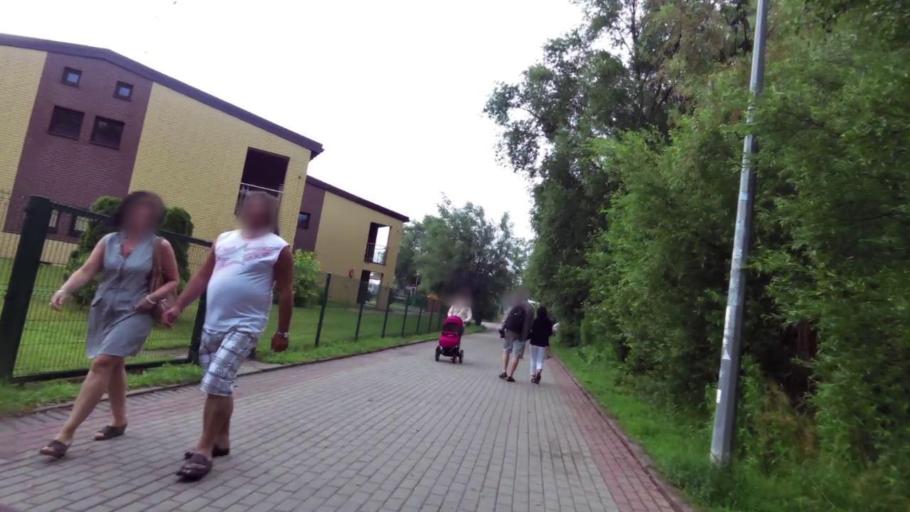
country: PL
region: West Pomeranian Voivodeship
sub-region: Powiat kolobrzeski
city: Ustronie Morskie
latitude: 54.2147
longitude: 15.7492
